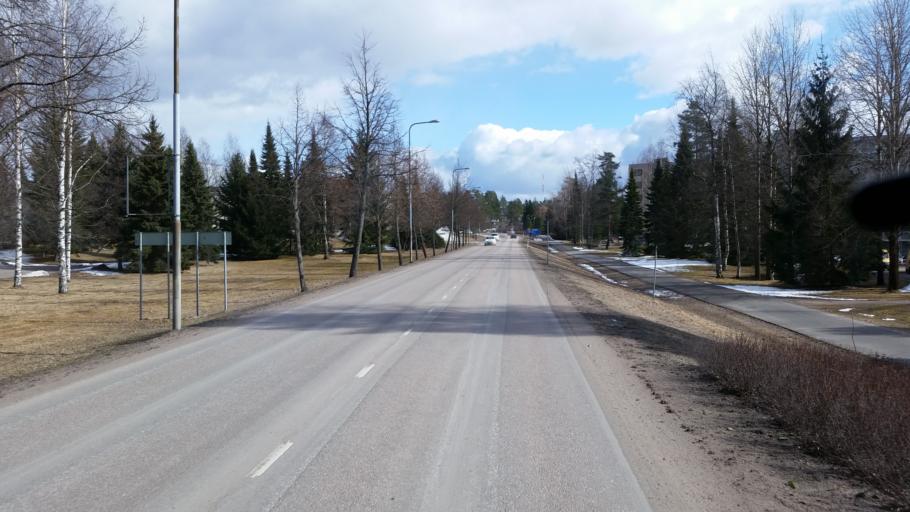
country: FI
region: South Karelia
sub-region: Imatra
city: Imatra
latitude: 61.1705
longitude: 28.7595
